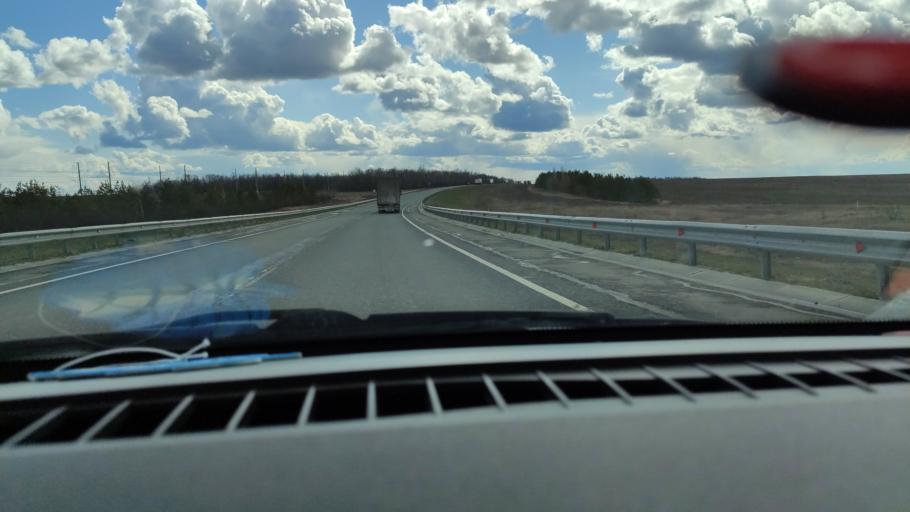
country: RU
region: Samara
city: Syzran'
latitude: 52.8719
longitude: 48.2856
